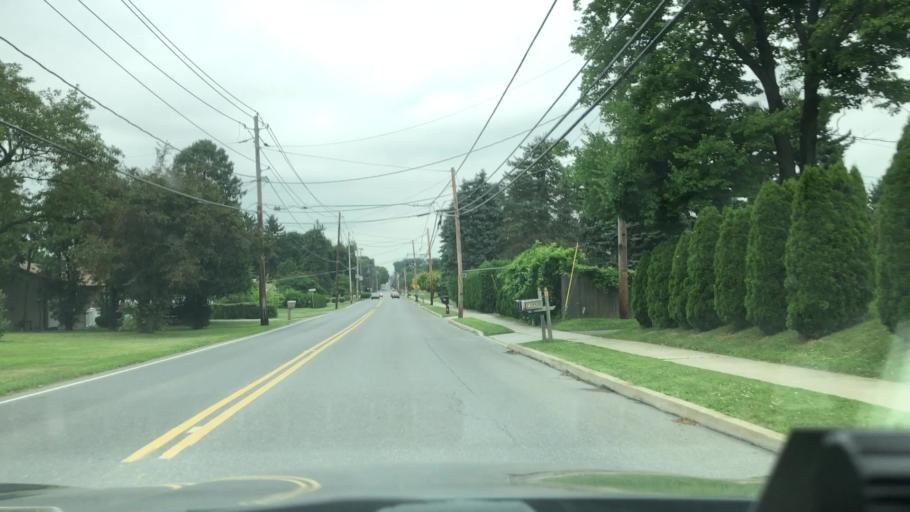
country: US
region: Pennsylvania
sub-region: Northampton County
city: Bethlehem
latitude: 40.6431
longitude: -75.3999
